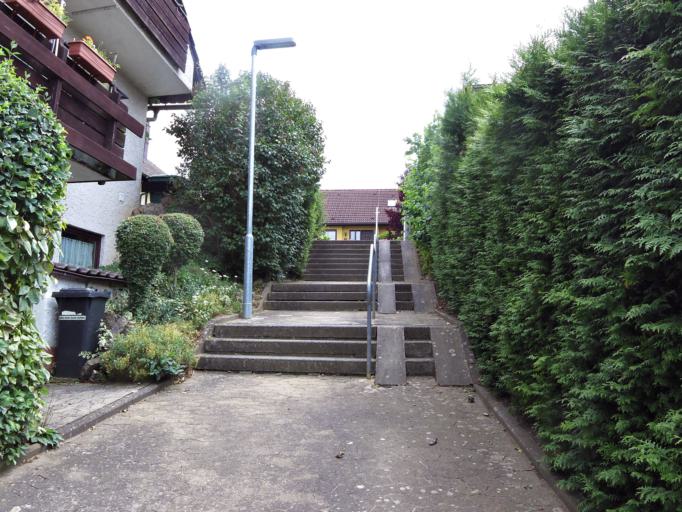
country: DE
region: Bavaria
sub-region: Regierungsbezirk Unterfranken
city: Eibelstadt
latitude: 49.7213
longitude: 9.9611
